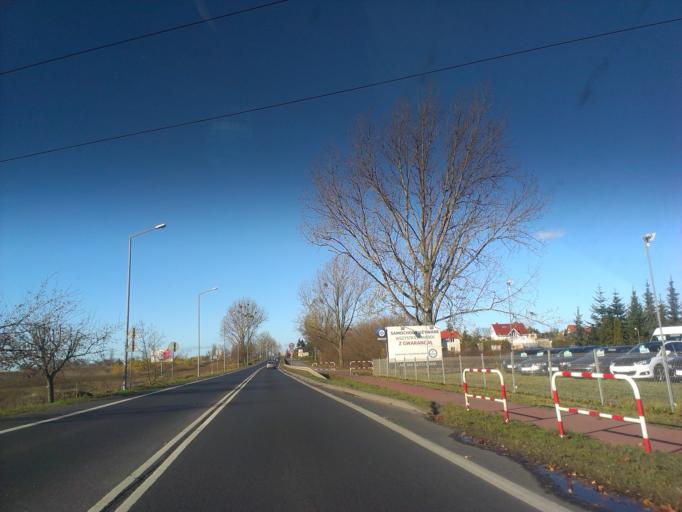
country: PL
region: Greater Poland Voivodeship
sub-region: Powiat poznanski
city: Zlotniki
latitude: 52.4875
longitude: 16.8523
